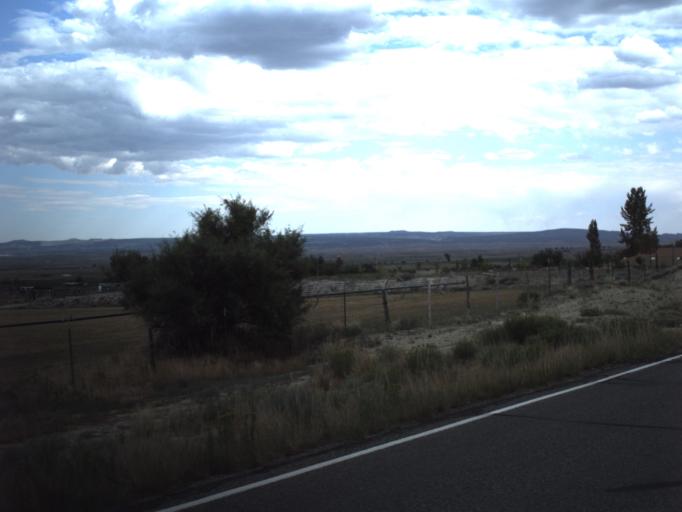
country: US
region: Utah
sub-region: Emery County
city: Huntington
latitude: 39.3882
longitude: -110.8525
